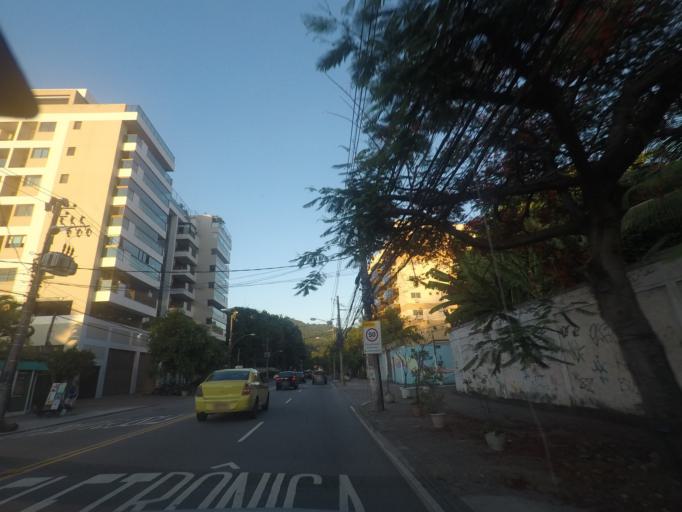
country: BR
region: Rio de Janeiro
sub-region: Rio De Janeiro
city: Rio de Janeiro
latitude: -22.9348
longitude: -43.3293
